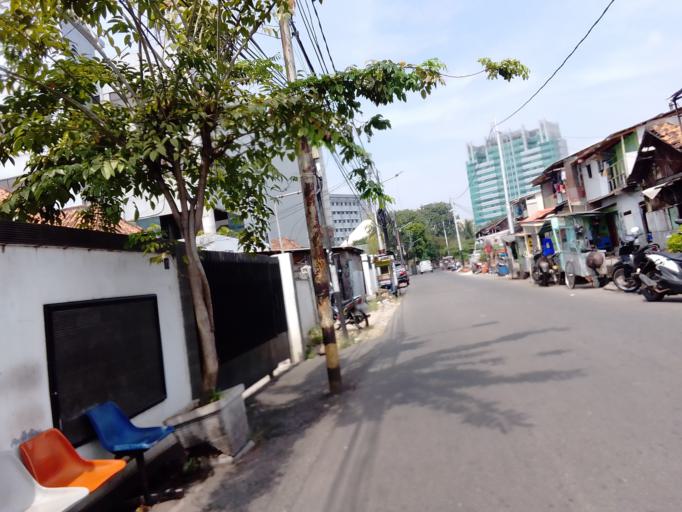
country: ID
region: Jakarta Raya
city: Jakarta
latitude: -6.1786
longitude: 106.8097
